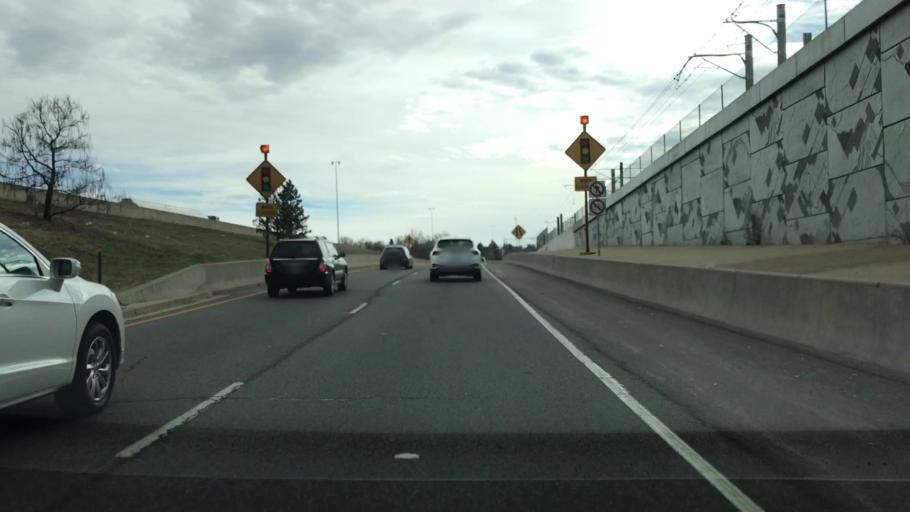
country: US
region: Colorado
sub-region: Arapahoe County
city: Glendale
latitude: 39.6674
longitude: -104.9264
